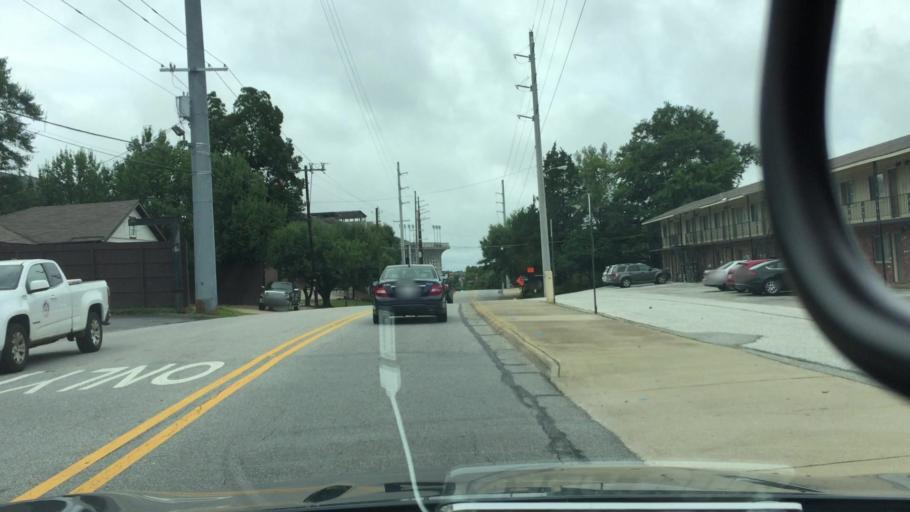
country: US
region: Alabama
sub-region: Lee County
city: Auburn
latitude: 32.6087
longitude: -85.4903
